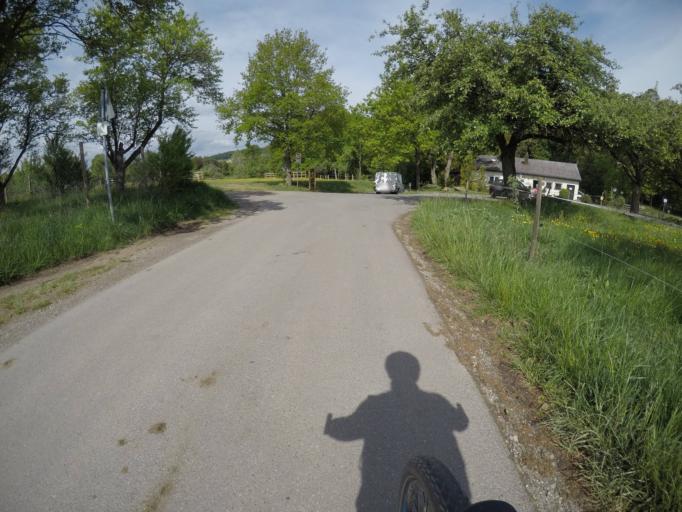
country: DE
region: Baden-Wuerttemberg
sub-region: Tuebingen Region
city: Tuebingen
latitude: 48.5400
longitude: 9.0255
